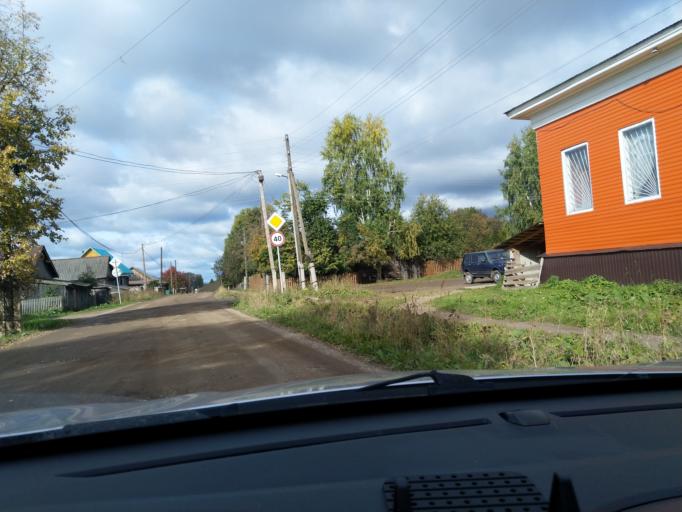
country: RU
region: Perm
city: Pozhva
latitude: 59.0881
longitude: 56.0769
